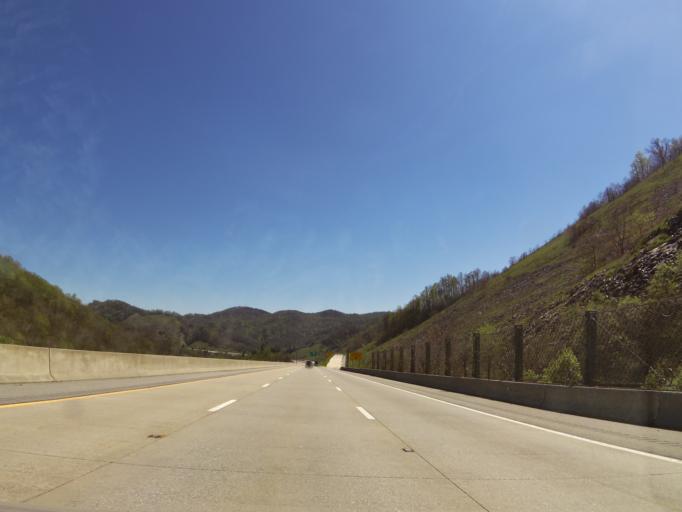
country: US
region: North Carolina
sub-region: Madison County
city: Mars Hill
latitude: 35.9250
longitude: -82.5564
